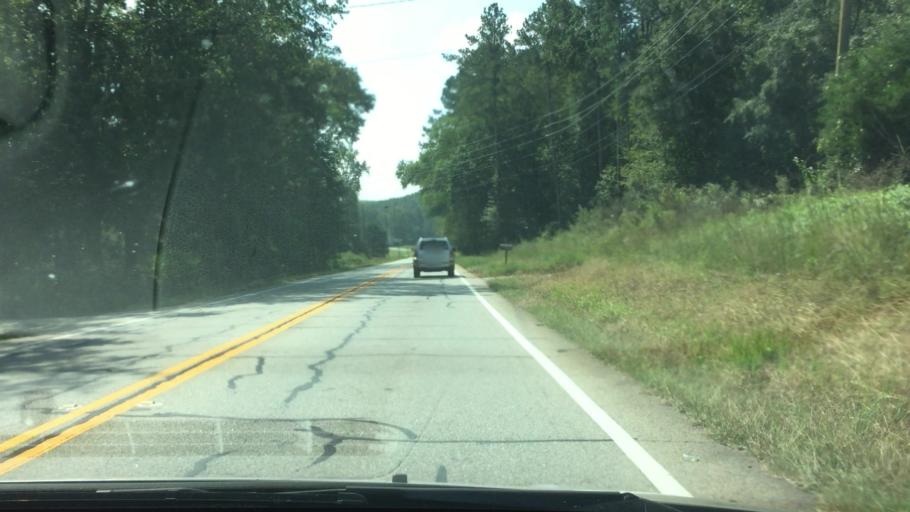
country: US
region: Georgia
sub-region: Henry County
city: McDonough
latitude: 33.5394
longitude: -84.1389
